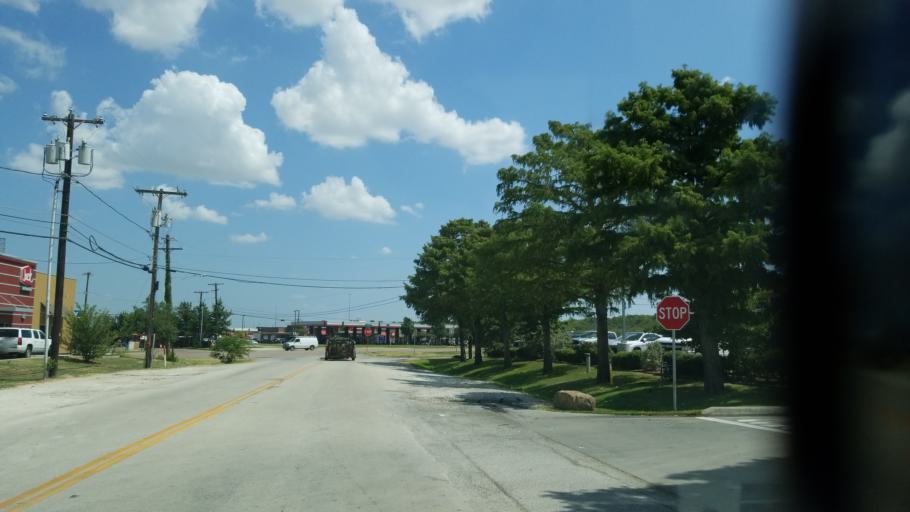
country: US
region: Texas
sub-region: Dallas County
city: Cockrell Hill
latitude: 32.7488
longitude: -96.9230
